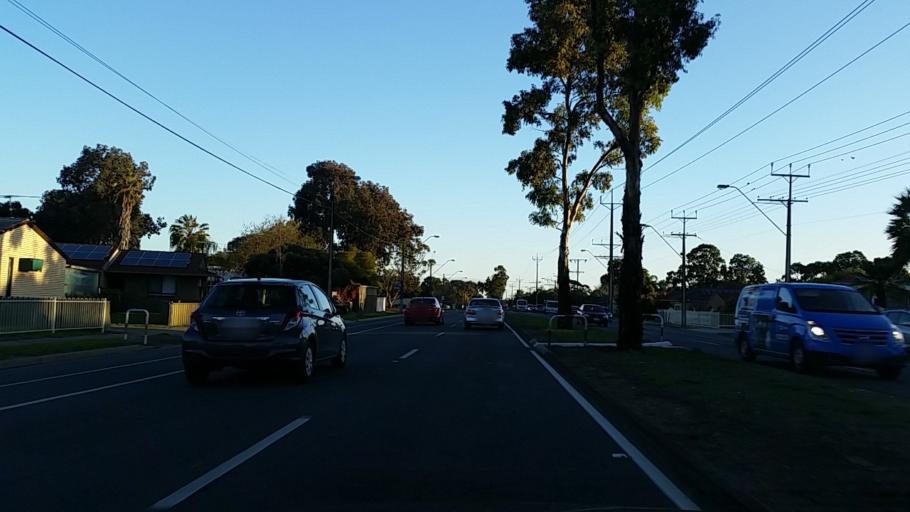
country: AU
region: South Australia
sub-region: Salisbury
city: Salisbury
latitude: -34.7741
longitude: 138.6309
